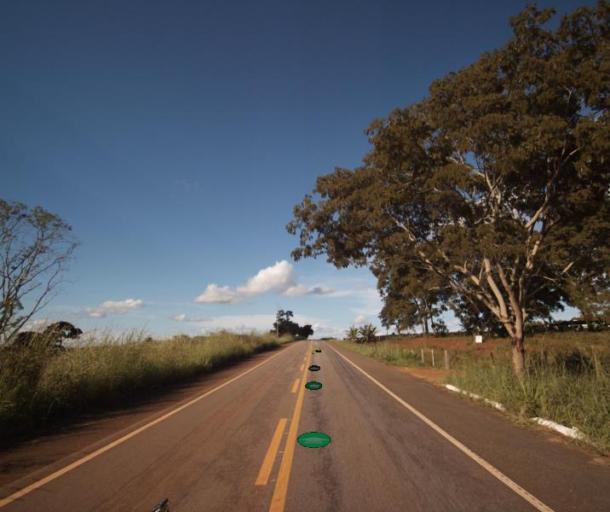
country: BR
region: Goias
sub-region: Itaberai
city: Itaberai
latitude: -15.9779
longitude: -49.6833
